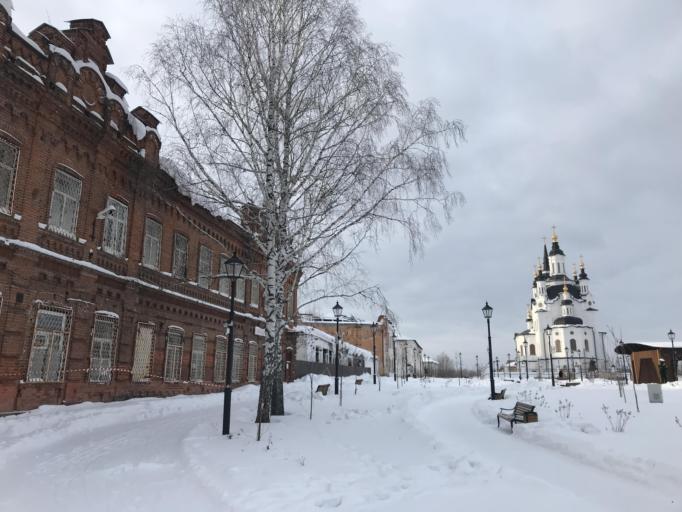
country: RU
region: Tjumen
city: Tobol'sk
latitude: 58.1956
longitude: 68.2460
